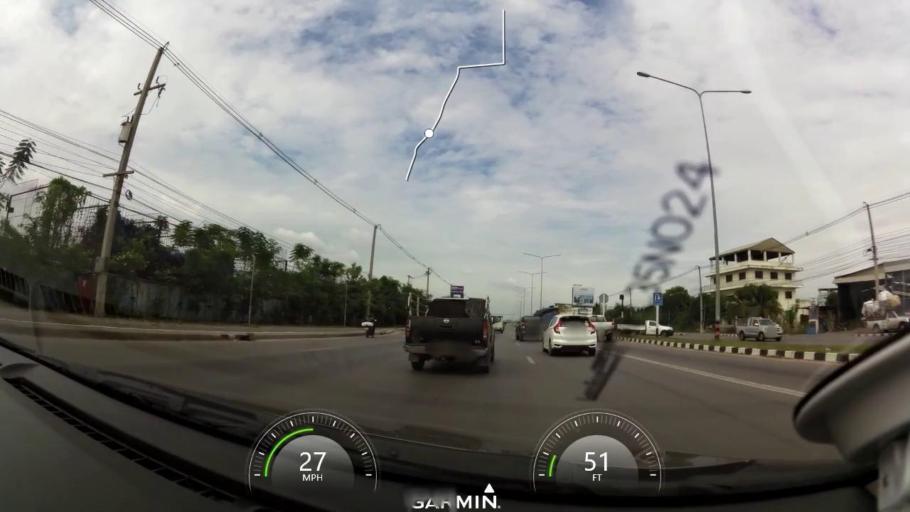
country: TH
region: Samut Sakhon
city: Krathum Baen
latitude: 13.6584
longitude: 100.3096
